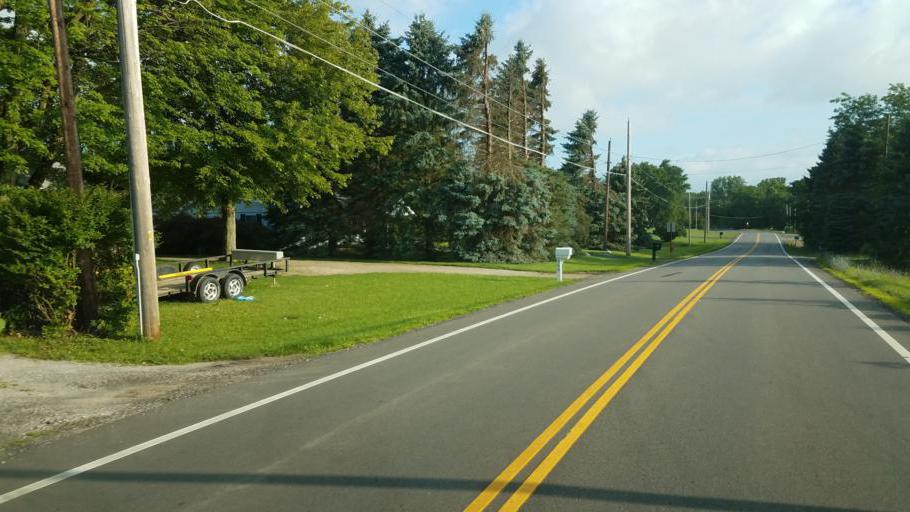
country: US
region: Ohio
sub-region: Richland County
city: Shelby
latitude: 40.8608
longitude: -82.6631
